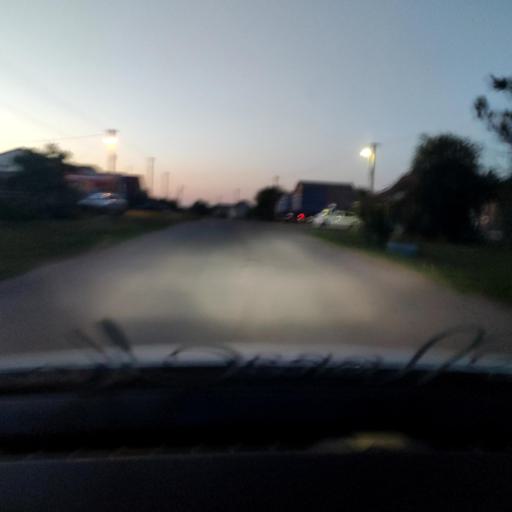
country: RU
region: Voronezj
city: Novovoronezh
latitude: 51.4143
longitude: 39.3225
